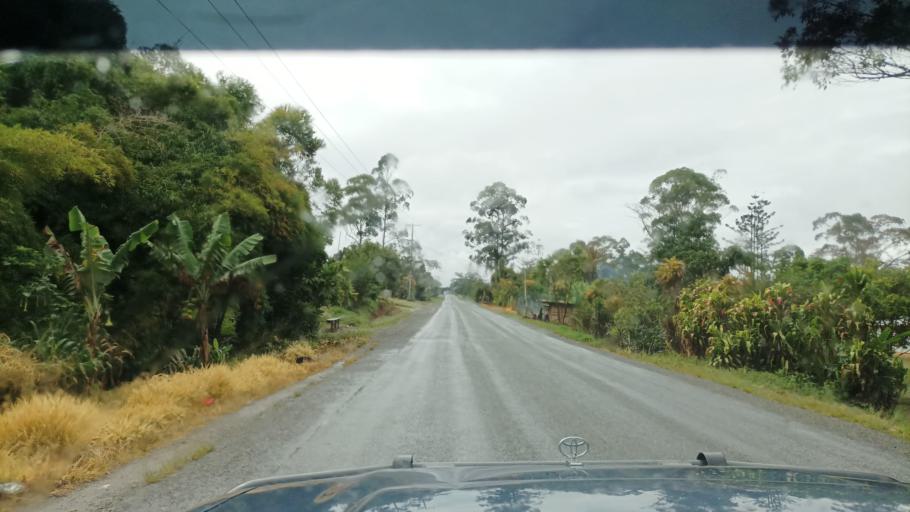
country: PG
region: Jiwaka
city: Minj
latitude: -5.8753
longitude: 144.6665
